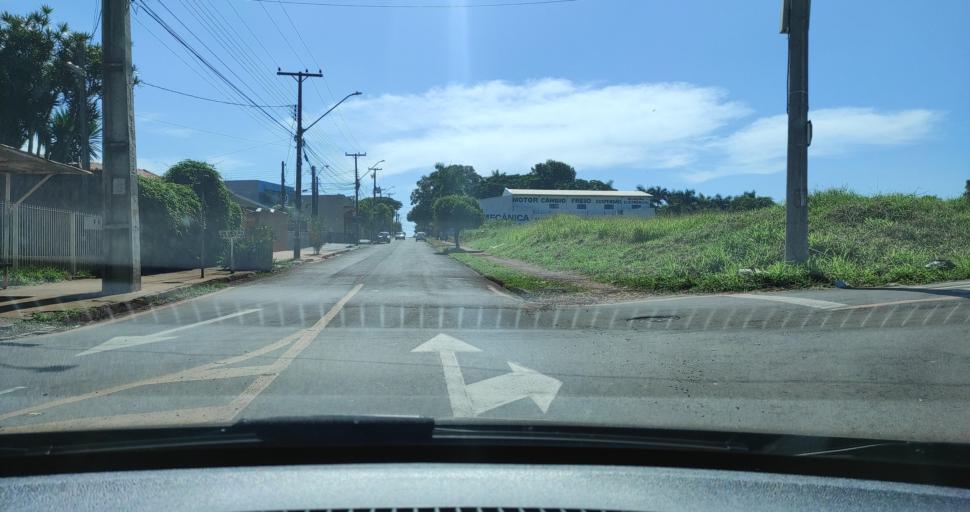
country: BR
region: Parana
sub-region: Ibipora
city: Ibipora
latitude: -23.2624
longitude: -51.0577
